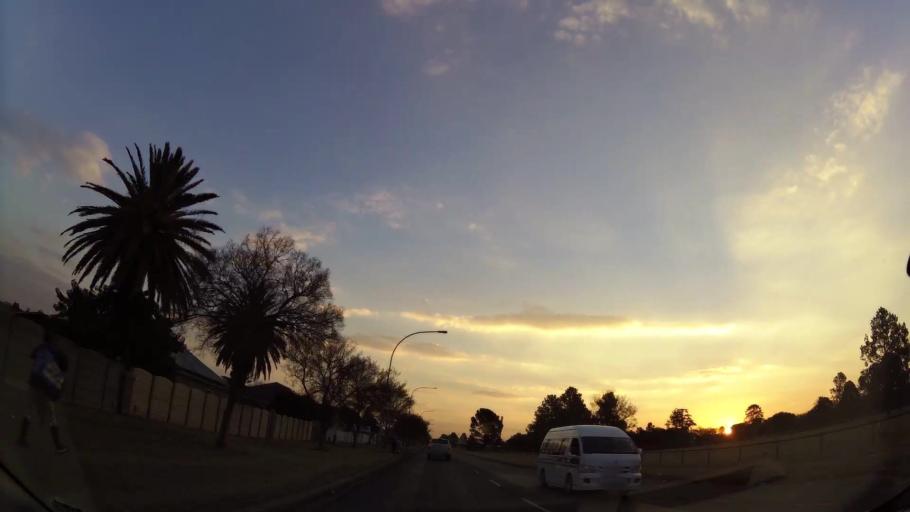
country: ZA
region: Gauteng
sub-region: Ekurhuleni Metropolitan Municipality
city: Benoni
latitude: -26.1753
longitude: 28.3251
